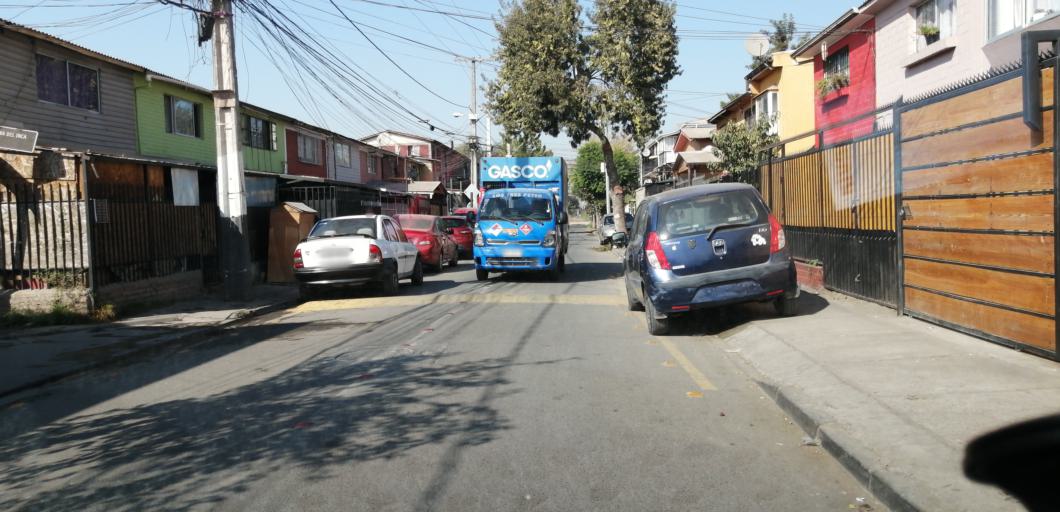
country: CL
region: Santiago Metropolitan
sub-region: Provincia de Santiago
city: Lo Prado
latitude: -33.4648
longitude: -70.7503
